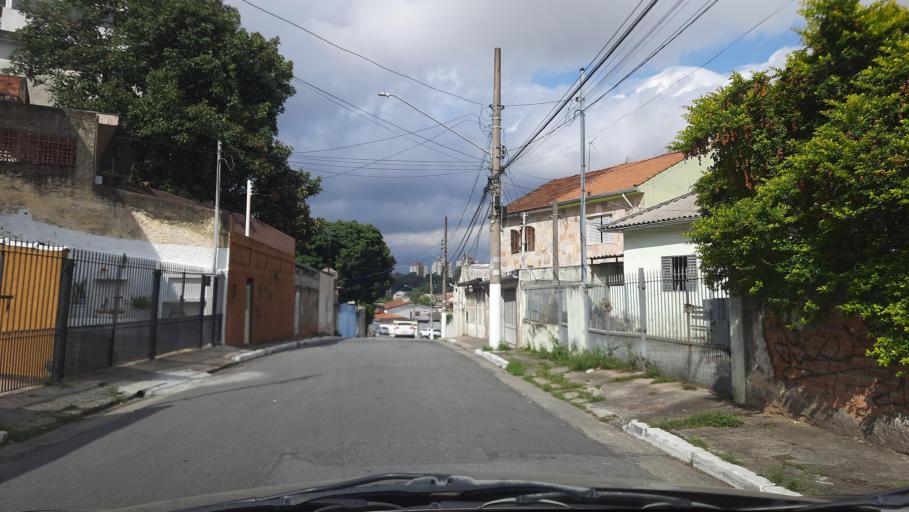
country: BR
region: Sao Paulo
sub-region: Sao Paulo
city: Sao Paulo
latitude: -23.4949
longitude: -46.6882
